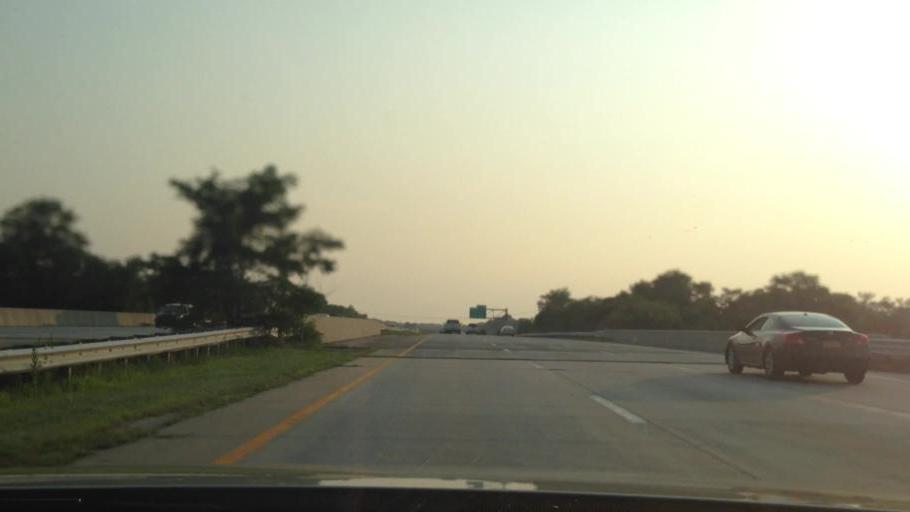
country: US
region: New York
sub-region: Suffolk County
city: Bohemia
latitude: 40.7611
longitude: -73.0974
